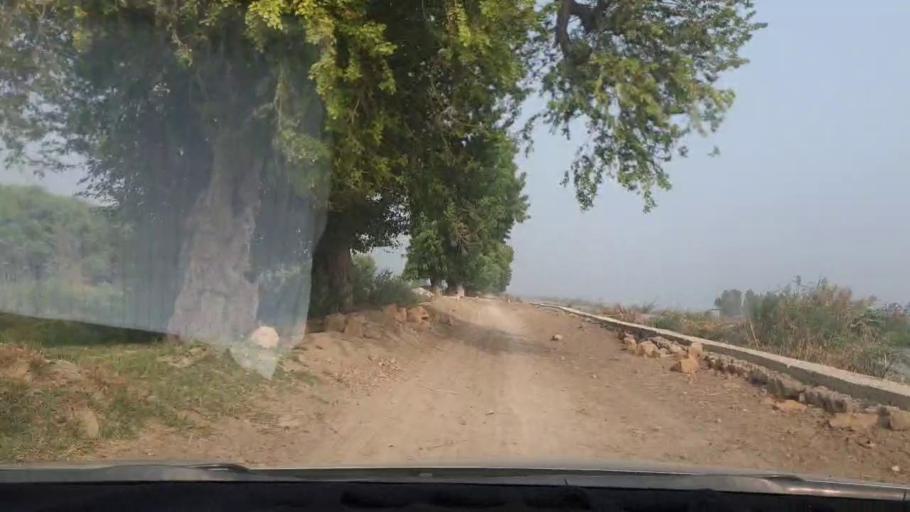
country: PK
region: Sindh
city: Matiari
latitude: 25.6734
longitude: 68.5579
